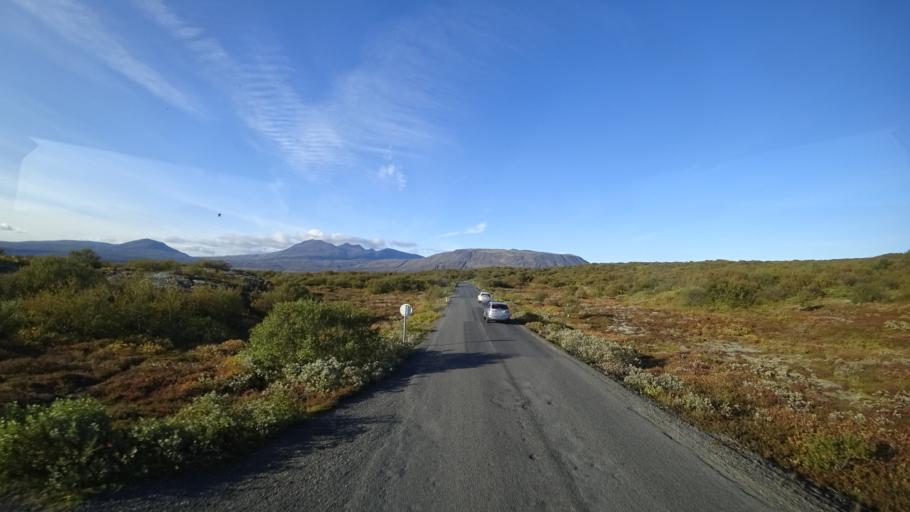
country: IS
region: South
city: Hveragerdi
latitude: 64.2557
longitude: -21.0278
